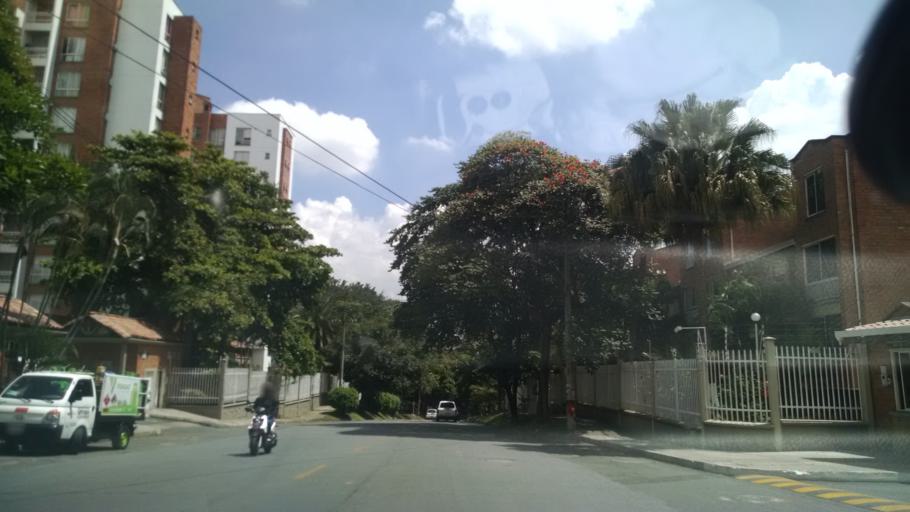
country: CO
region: Antioquia
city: Itagui
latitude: 6.2220
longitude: -75.6029
